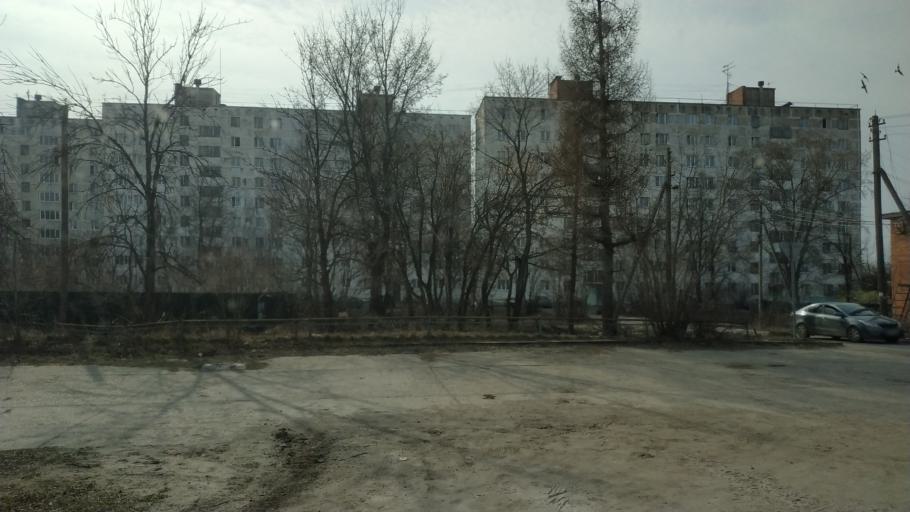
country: RU
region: Moskovskaya
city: Beloozerskiy
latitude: 55.4477
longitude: 38.4803
